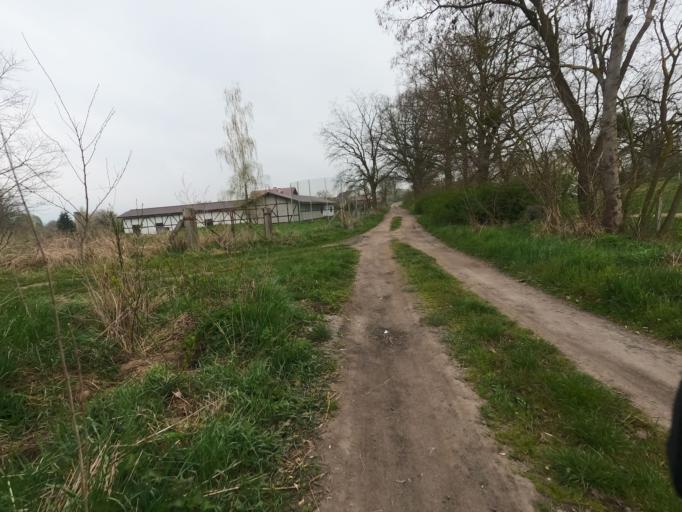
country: PL
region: West Pomeranian Voivodeship
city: Trzcinsko Zdroj
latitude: 52.9157
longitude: 14.5973
